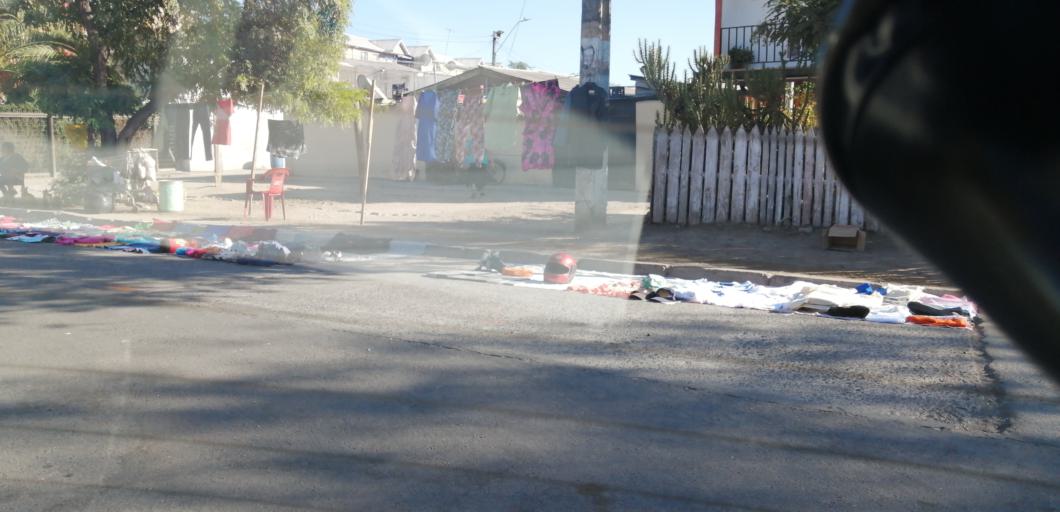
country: CL
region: Santiago Metropolitan
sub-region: Provincia de Santiago
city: Lo Prado
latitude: -33.4357
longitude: -70.7613
